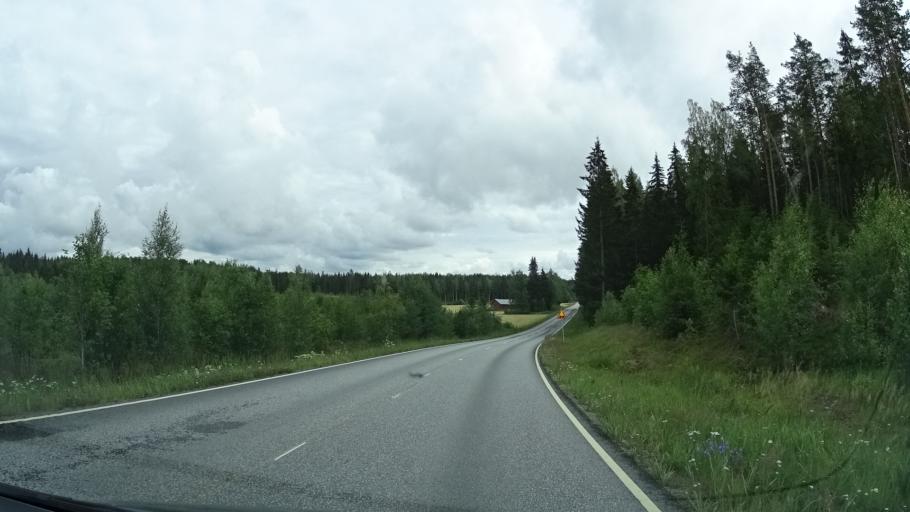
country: FI
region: Haeme
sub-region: Forssa
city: Humppila
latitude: 61.0963
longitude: 23.3567
